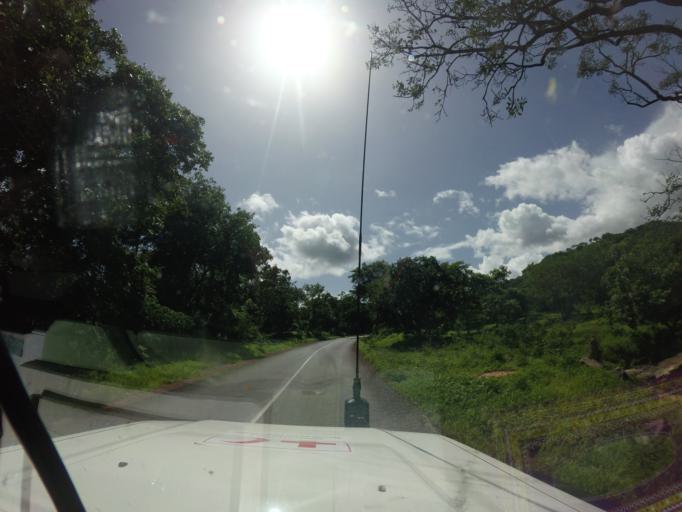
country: GN
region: Mamou
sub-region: Mamou Prefecture
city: Mamou
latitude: 10.2653
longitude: -11.8938
